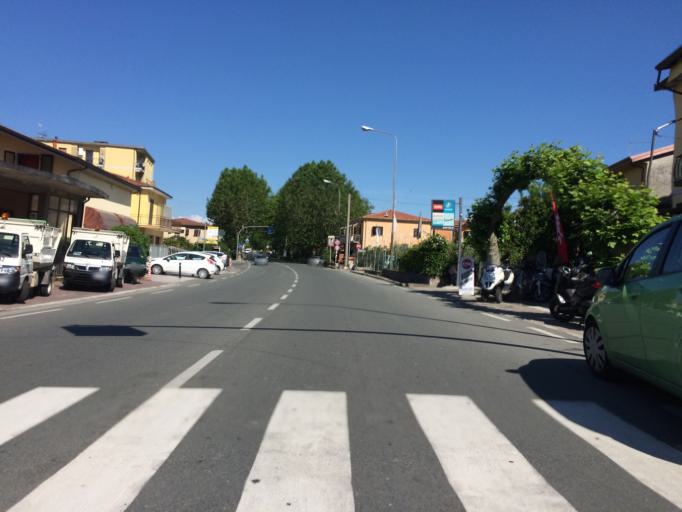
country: IT
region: Liguria
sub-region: Provincia di La Spezia
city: Colombiera-Molicciara
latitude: 44.0848
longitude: 10.0064
